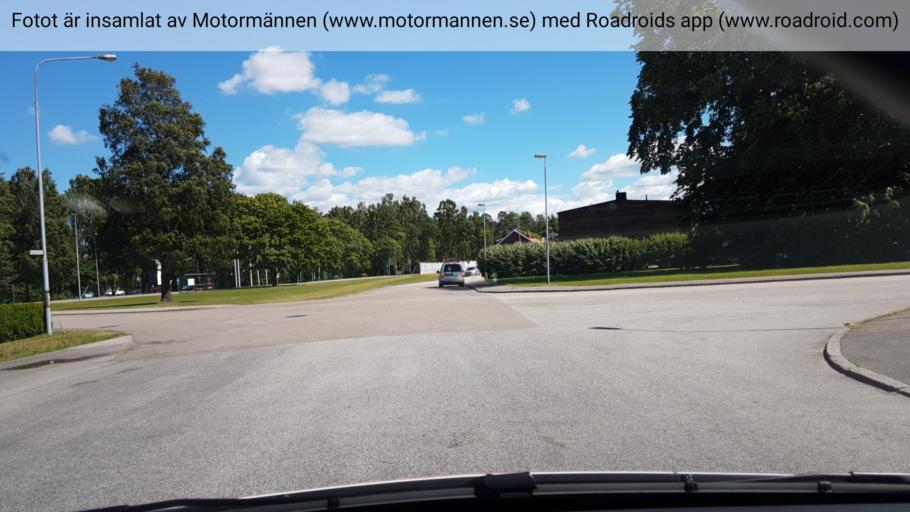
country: SE
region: Vaestra Goetaland
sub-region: Lidkopings Kommun
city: Lidkoping
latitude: 58.5129
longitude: 13.1358
